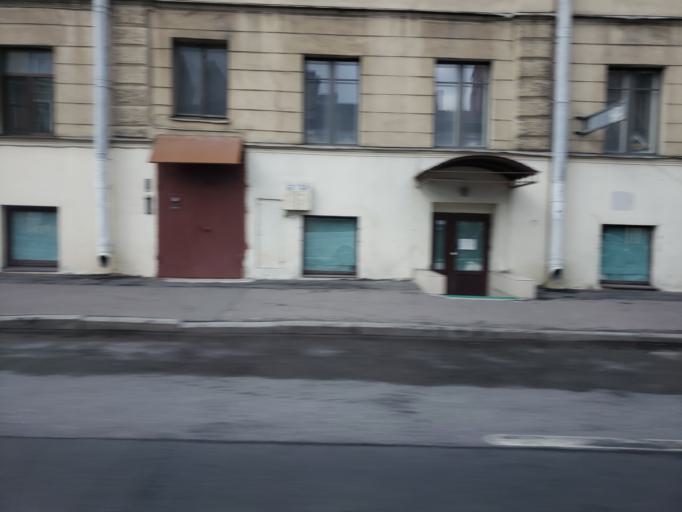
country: RU
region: St.-Petersburg
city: Admiralteisky
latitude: 59.9367
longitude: 30.2826
